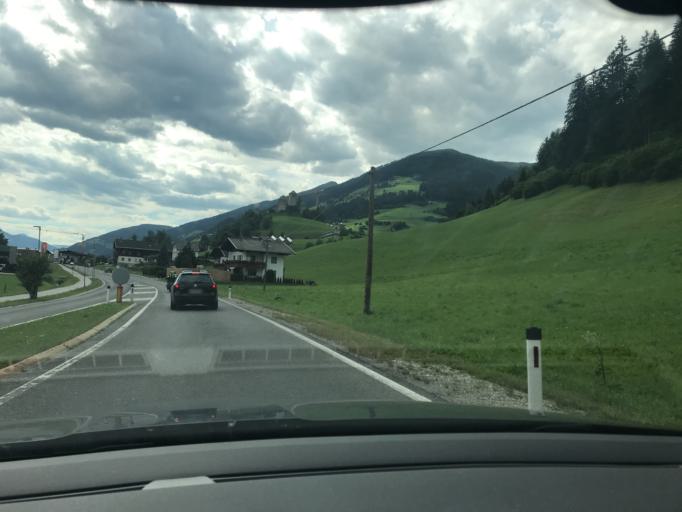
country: AT
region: Tyrol
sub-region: Politischer Bezirk Lienz
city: Heinfels
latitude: 46.7499
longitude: 12.4486
